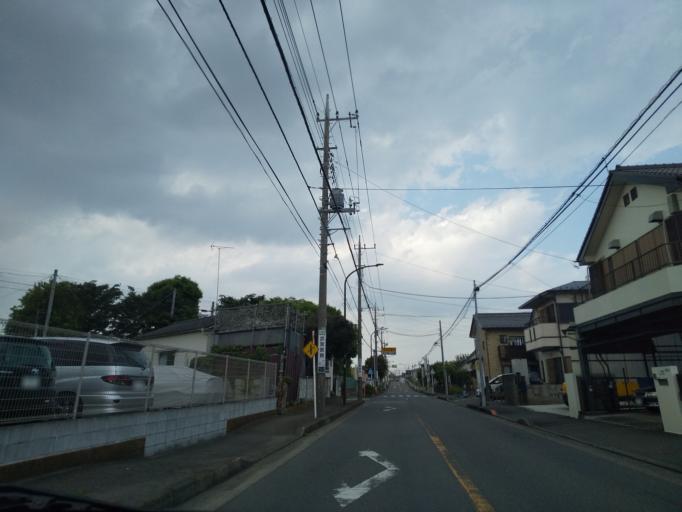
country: JP
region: Tokyo
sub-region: Machida-shi
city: Machida
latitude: 35.5295
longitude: 139.4128
